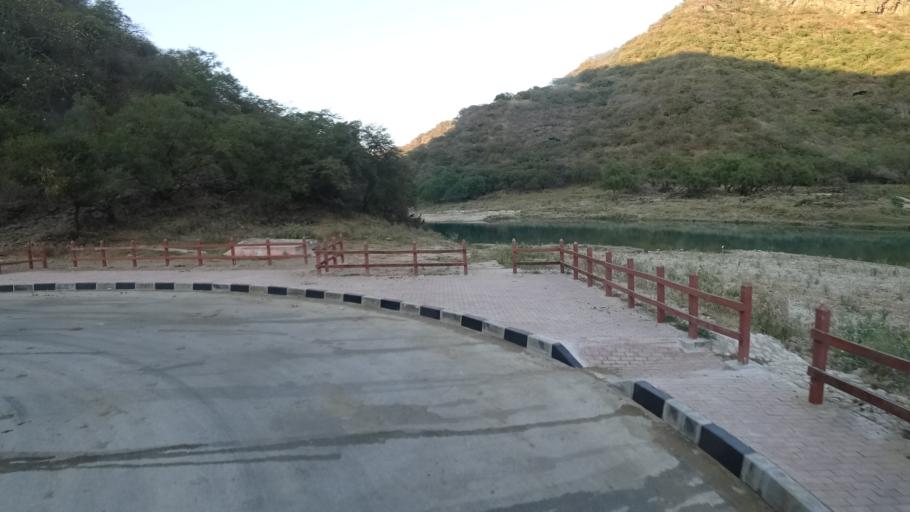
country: OM
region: Zufar
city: Salalah
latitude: 17.1048
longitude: 54.4527
